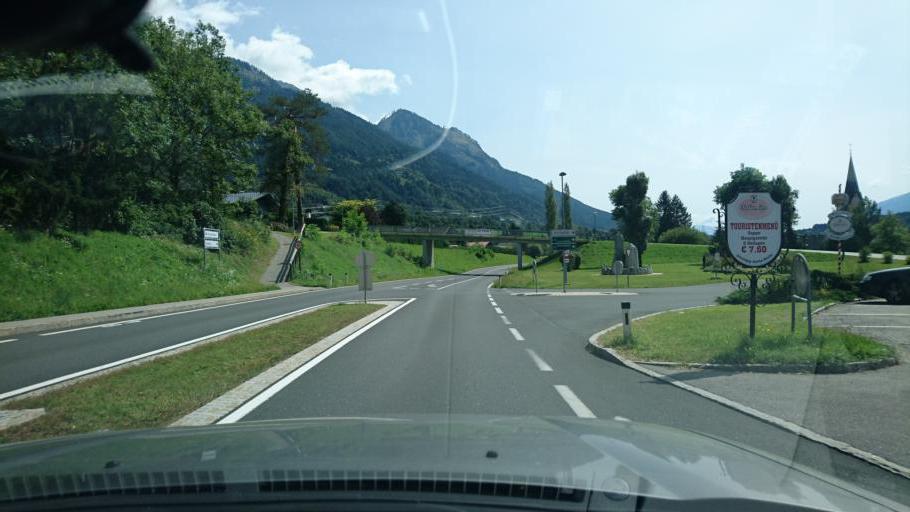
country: AT
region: Carinthia
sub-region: Politischer Bezirk Spittal an der Drau
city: Muhldorf
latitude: 46.8762
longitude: 13.3042
